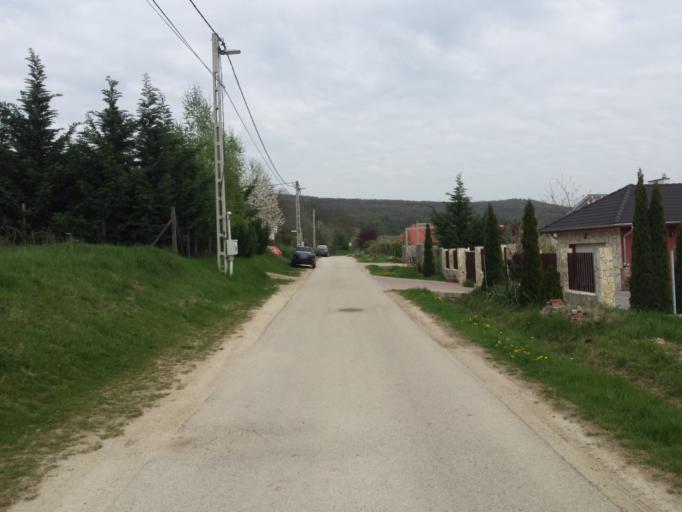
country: HU
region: Fejer
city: Velence
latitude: 47.2604
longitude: 18.6184
